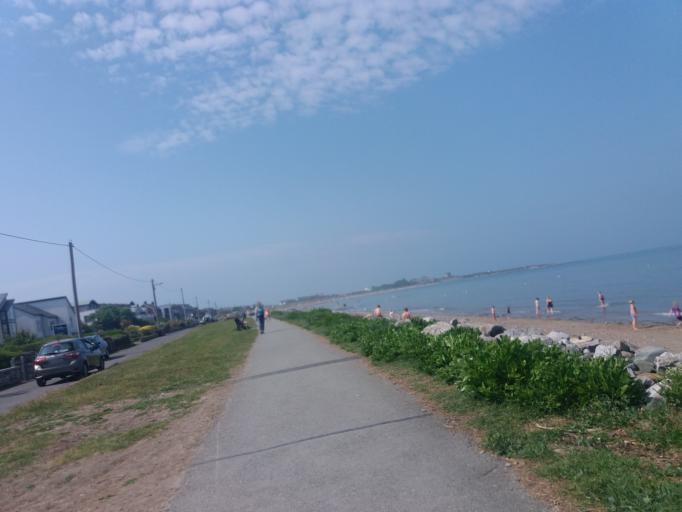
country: IE
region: Leinster
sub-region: Fingal County
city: Skerries
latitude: 53.5744
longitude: -6.1018
